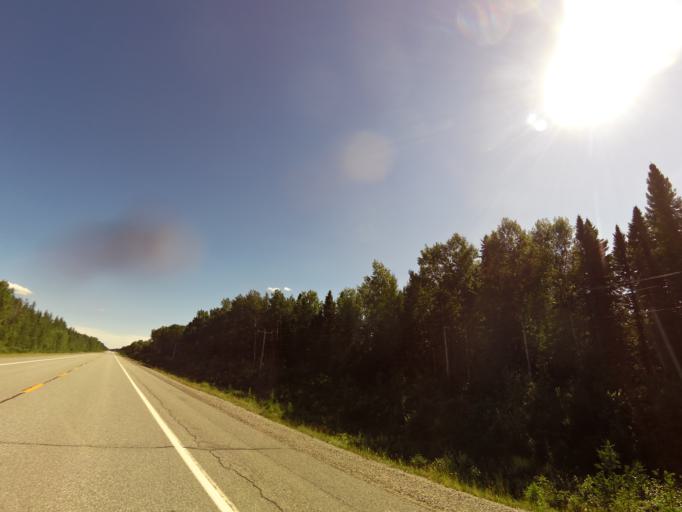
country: CA
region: Quebec
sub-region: Abitibi-Temiscamingue
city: Val-d'Or
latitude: 47.9607
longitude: -77.3608
